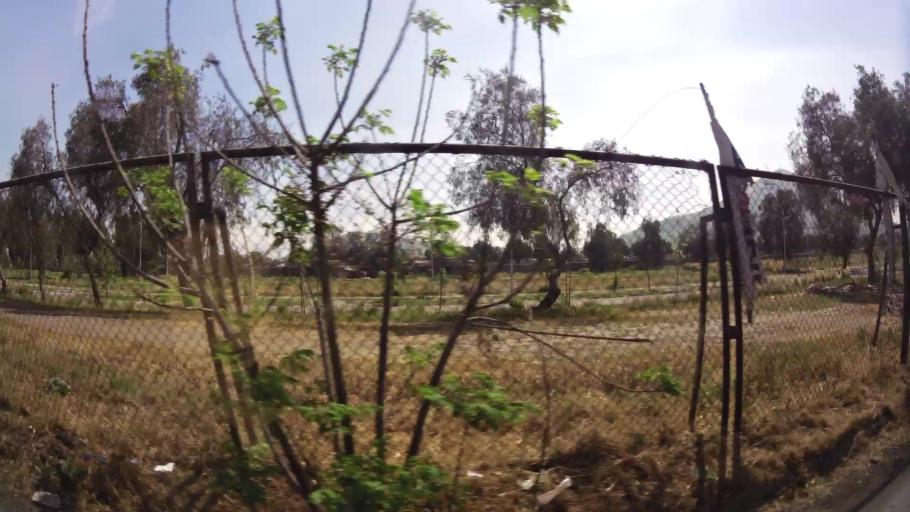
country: CL
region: Santiago Metropolitan
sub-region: Provincia de Santiago
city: Lo Prado
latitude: -33.4102
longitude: -70.7143
